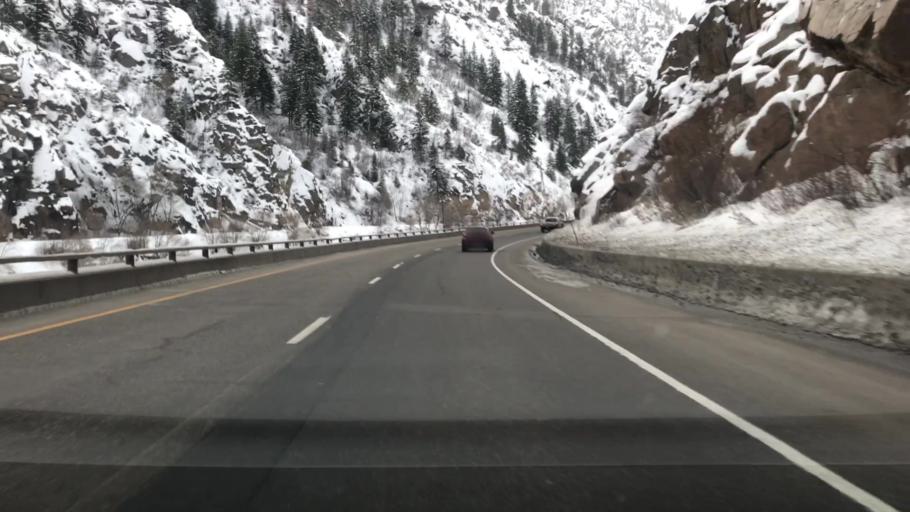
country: US
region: Colorado
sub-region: Garfield County
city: Glenwood Springs
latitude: 39.5718
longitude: -107.2242
